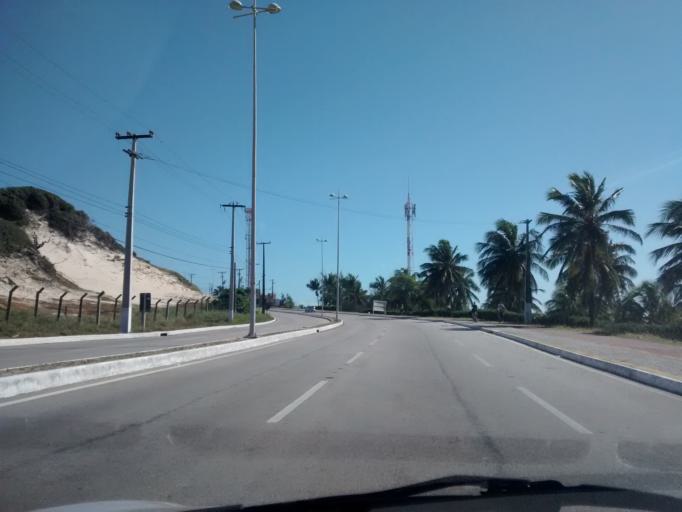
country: BR
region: Rio Grande do Norte
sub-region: Natal
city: Natal
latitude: -5.8308
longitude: -35.1828
